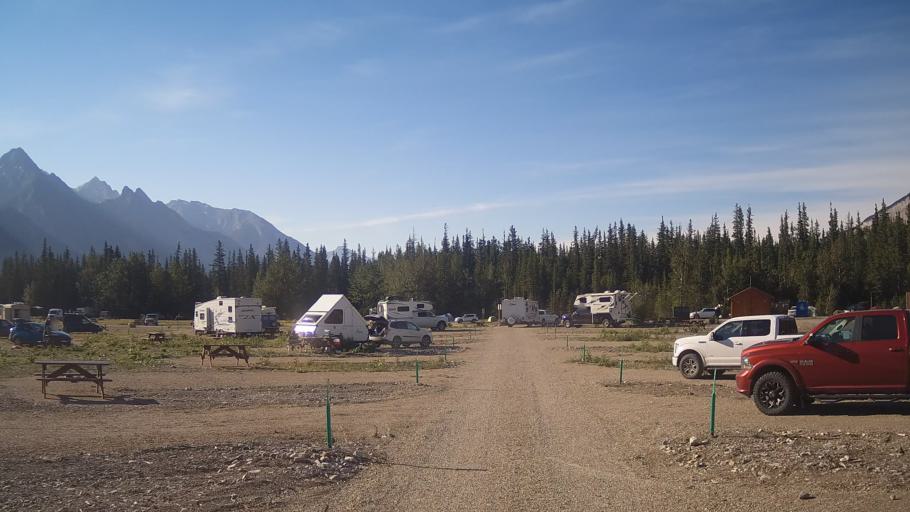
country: CA
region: Alberta
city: Jasper Park Lodge
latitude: 53.0165
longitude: -118.0826
